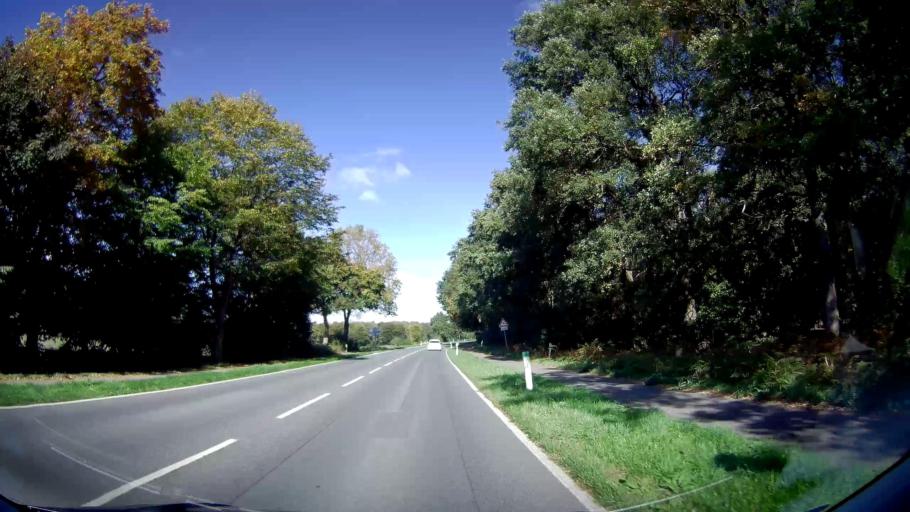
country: DE
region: North Rhine-Westphalia
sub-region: Regierungsbezirk Dusseldorf
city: Dinslaken
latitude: 51.6060
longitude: 6.7555
